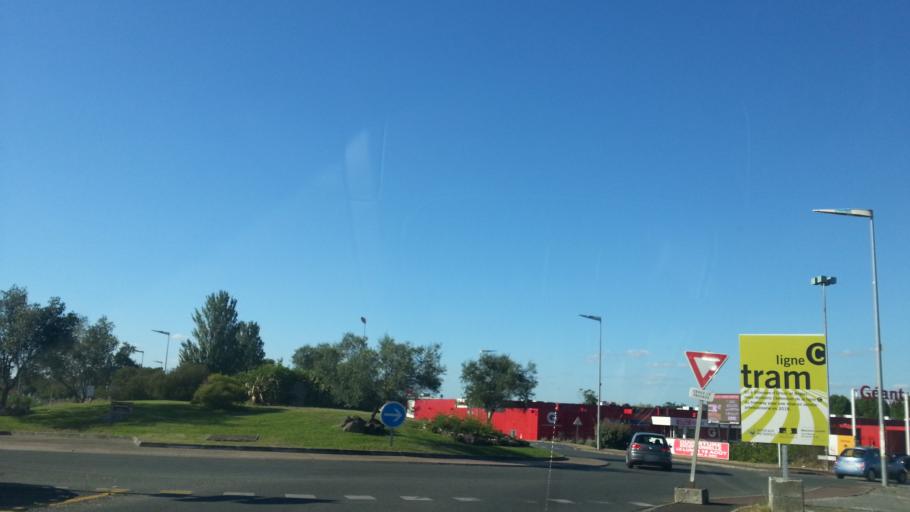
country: FR
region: Aquitaine
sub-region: Departement de la Gironde
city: Villenave-d'Ornon
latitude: 44.7745
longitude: -0.5646
